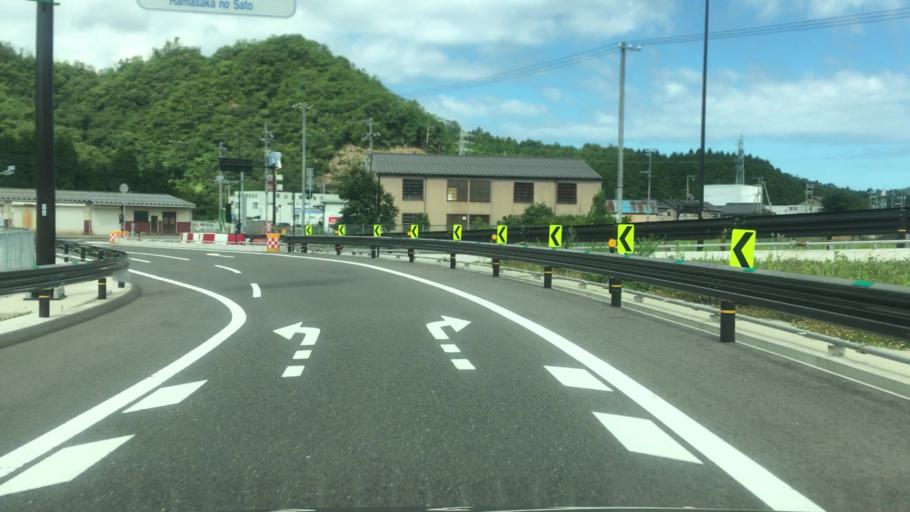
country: JP
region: Tottori
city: Tottori
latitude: 35.6115
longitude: 134.4704
